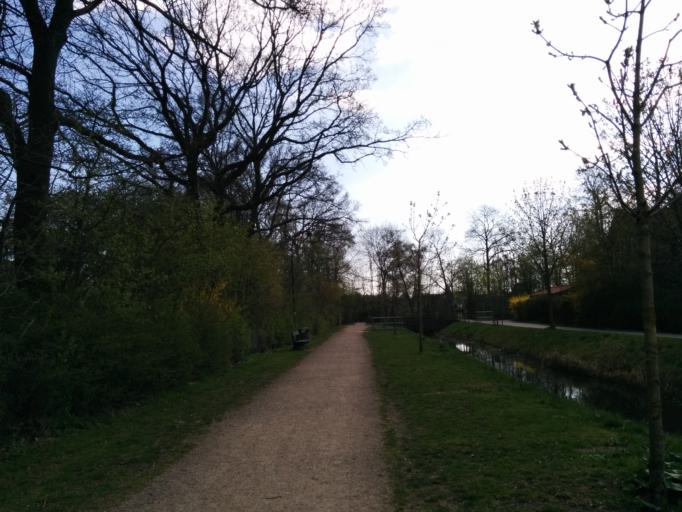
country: DK
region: Capital Region
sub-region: Frederiksberg Kommune
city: Frederiksberg
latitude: 55.7279
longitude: 12.5352
